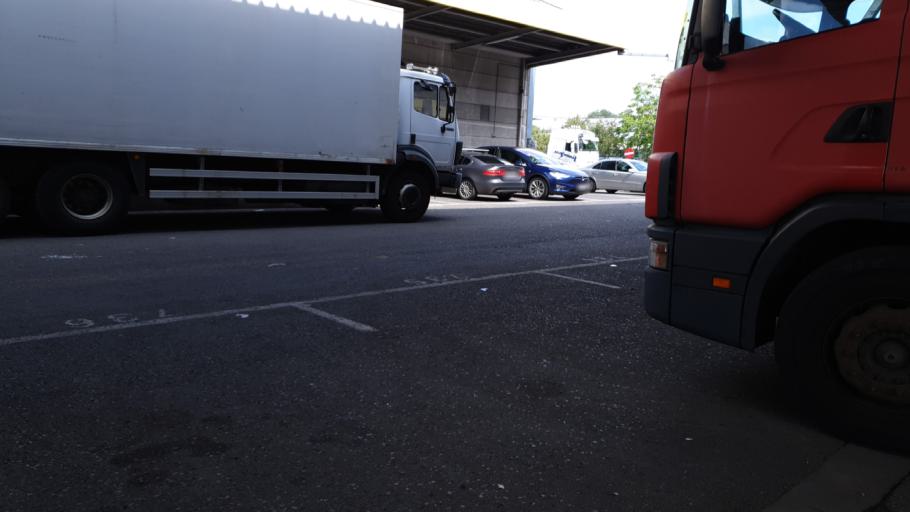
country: BE
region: Brussels Capital
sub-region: Bruxelles-Capitale
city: Brussels
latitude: 50.8747
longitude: 4.3667
